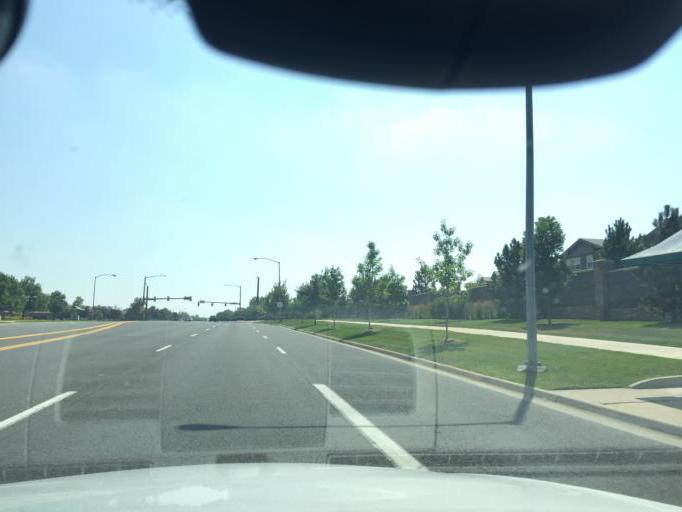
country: US
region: Colorado
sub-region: Adams County
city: Northglenn
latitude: 39.8996
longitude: -105.0271
